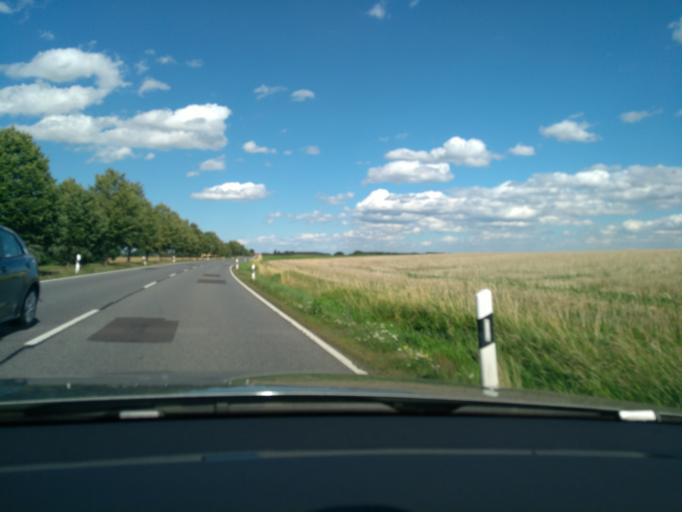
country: DE
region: Saxony
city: Demitz-Thumitz
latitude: 51.1566
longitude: 14.2553
